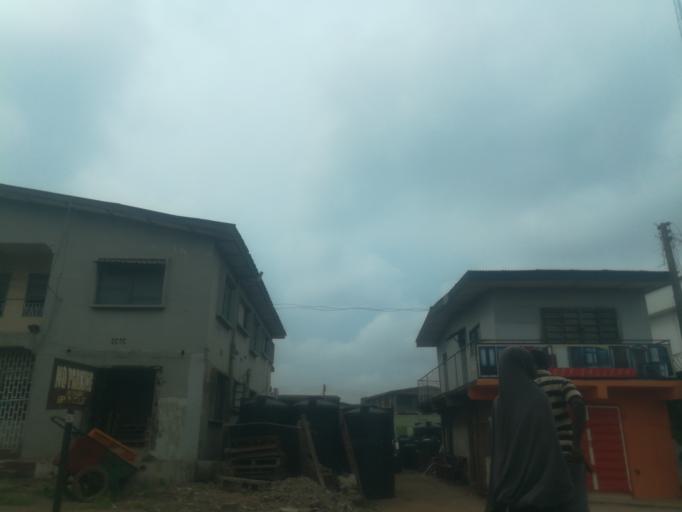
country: NG
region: Oyo
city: Ibadan
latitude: 7.4031
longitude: 3.9408
